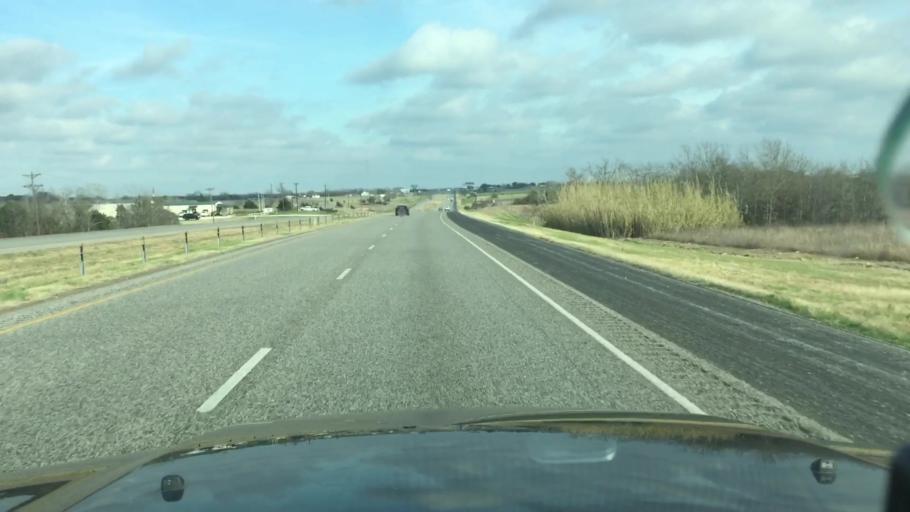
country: US
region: Texas
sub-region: Washington County
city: Brenham
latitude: 30.1388
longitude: -96.3144
